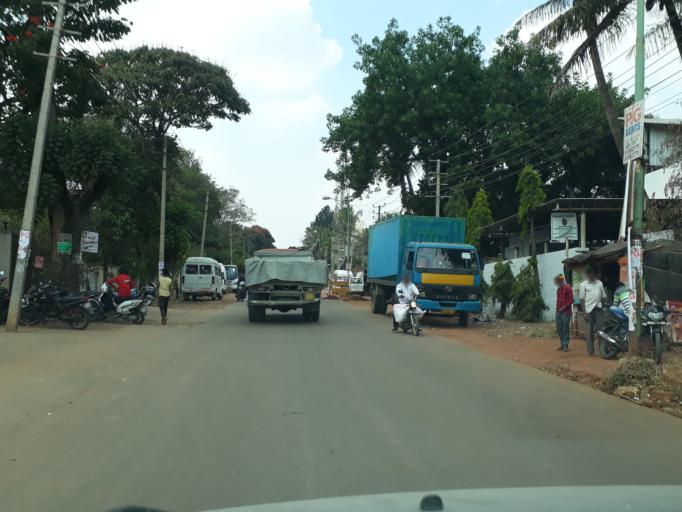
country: IN
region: Karnataka
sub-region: Bangalore Urban
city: Anekal
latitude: 12.8142
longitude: 77.6789
